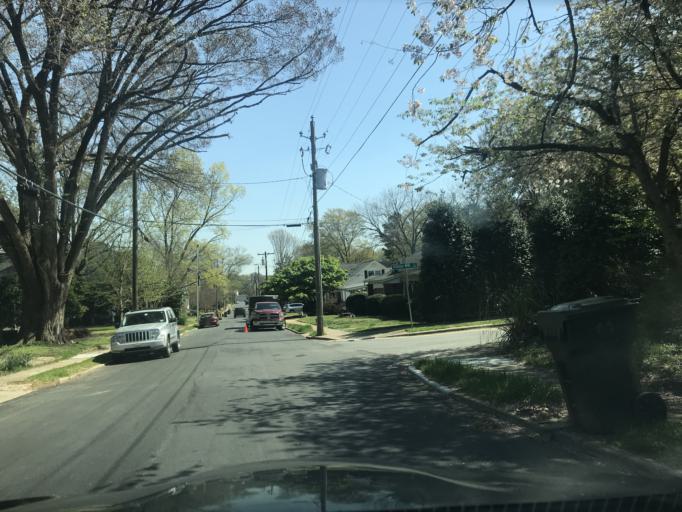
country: US
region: North Carolina
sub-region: Wake County
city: West Raleigh
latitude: 35.8061
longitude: -78.6385
